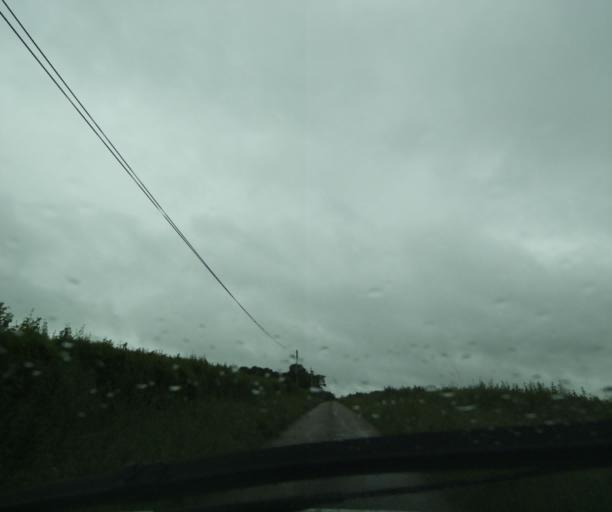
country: FR
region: Bourgogne
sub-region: Departement de Saone-et-Loire
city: Charolles
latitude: 46.4850
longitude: 4.2920
